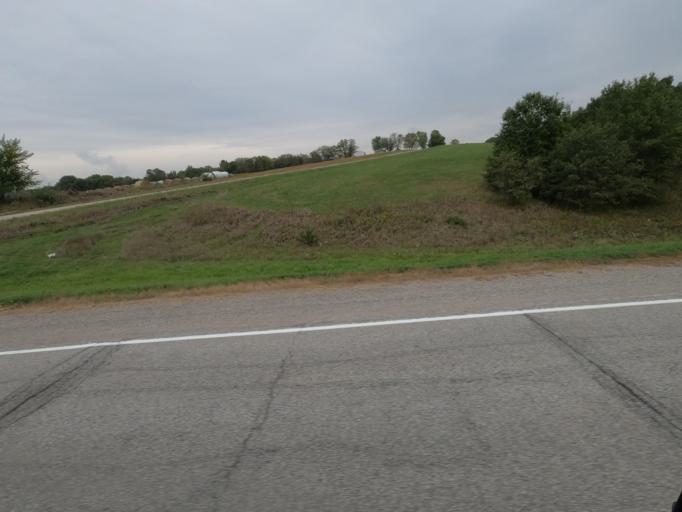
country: US
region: Iowa
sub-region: Van Buren County
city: Keosauqua
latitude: 40.8348
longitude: -91.9723
